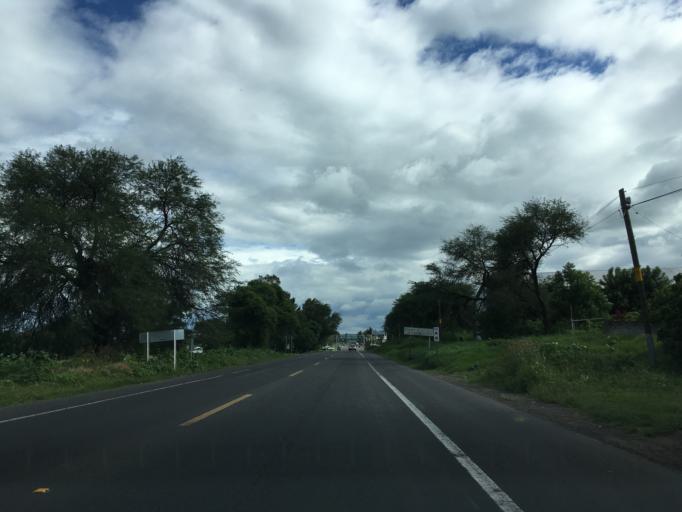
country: MX
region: Guanajuato
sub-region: Moroleon
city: Rinconadas del Bosque
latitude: 20.0939
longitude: -101.1588
